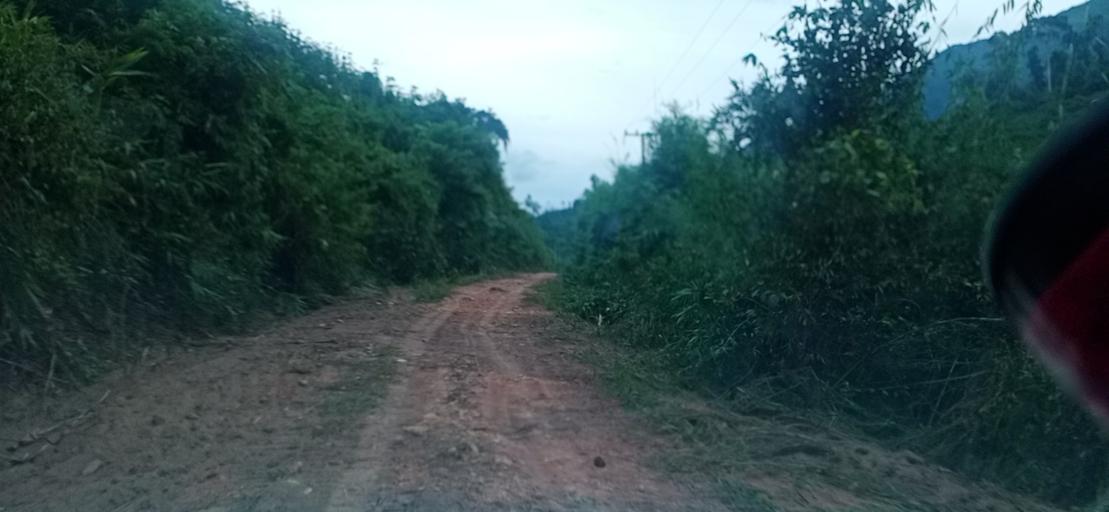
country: TH
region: Changwat Bueng Kan
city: Pak Khat
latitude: 18.5595
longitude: 103.2460
